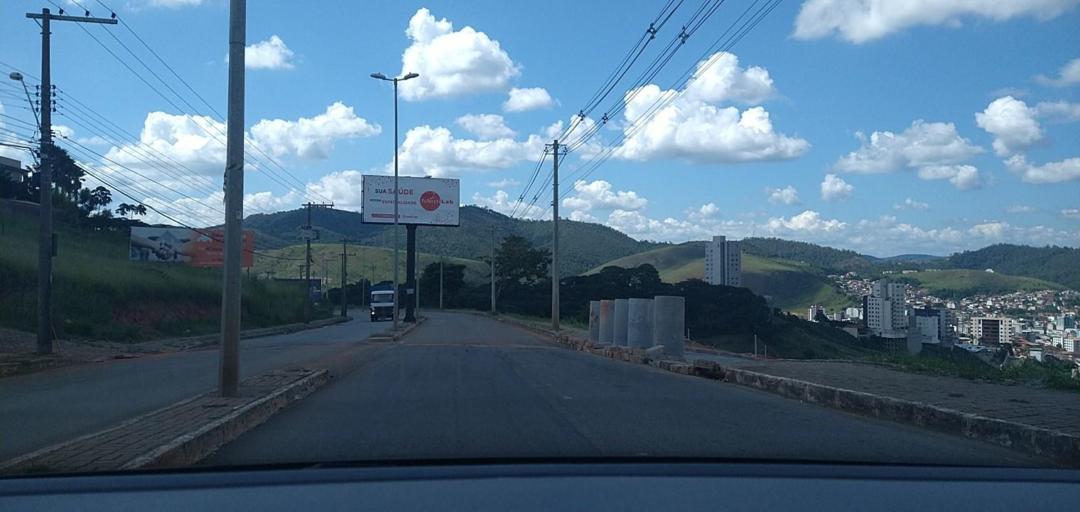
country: BR
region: Minas Gerais
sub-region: Joao Monlevade
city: Joao Monlevade
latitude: -19.8212
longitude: -43.1896
